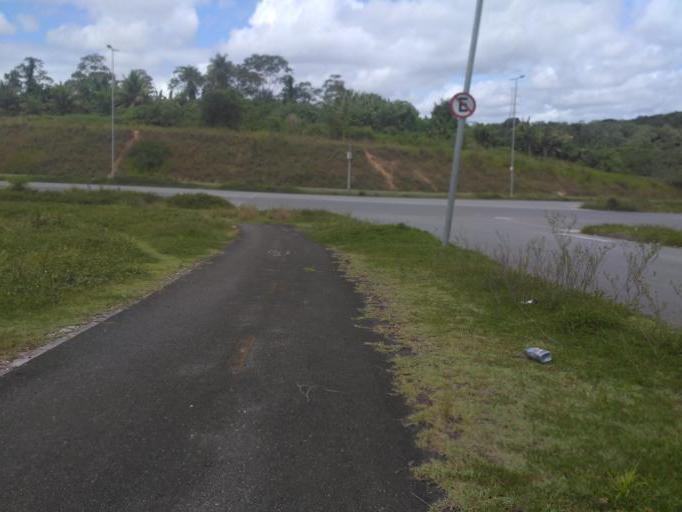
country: BR
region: Pernambuco
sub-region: Sao Lourenco Da Mata
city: Sao Lourenco da Mata
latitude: -8.0422
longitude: -34.9975
